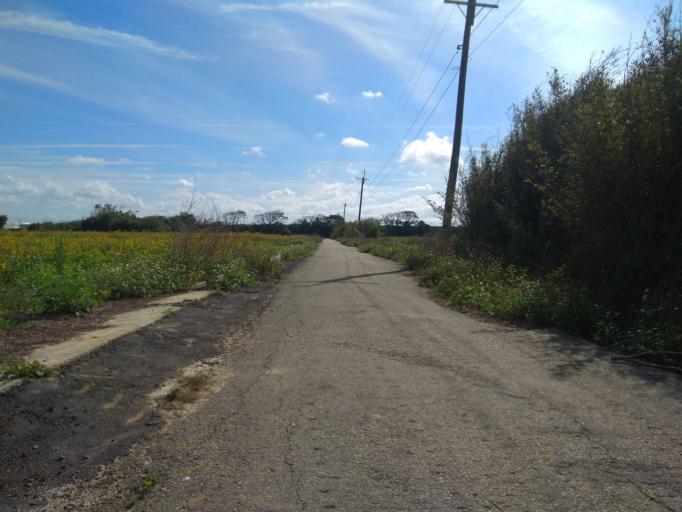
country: TW
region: Taiwan
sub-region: Hsinchu
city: Zhubei
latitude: 25.0170
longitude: 121.0657
